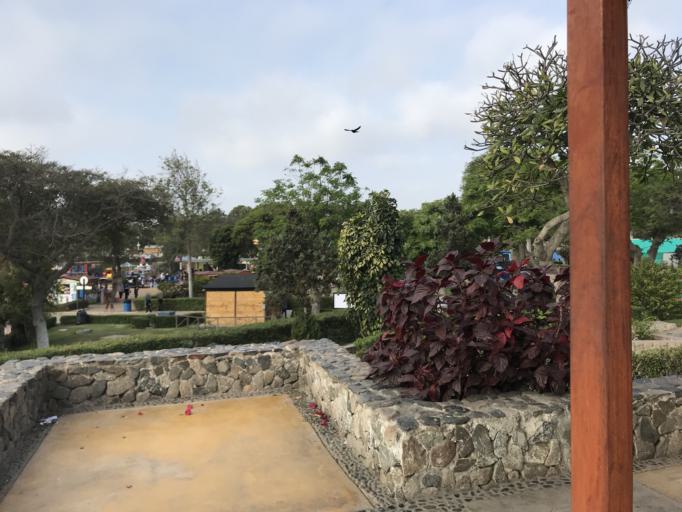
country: PE
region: Callao
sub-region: Callao
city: Callao
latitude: -12.0697
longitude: -77.0885
